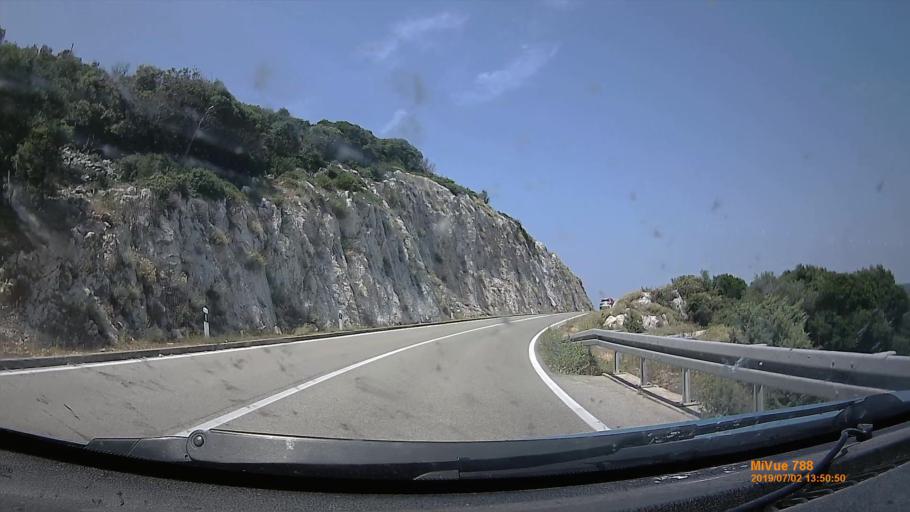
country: HR
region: Primorsko-Goranska
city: Mali Losinj
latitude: 44.5995
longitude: 14.4069
